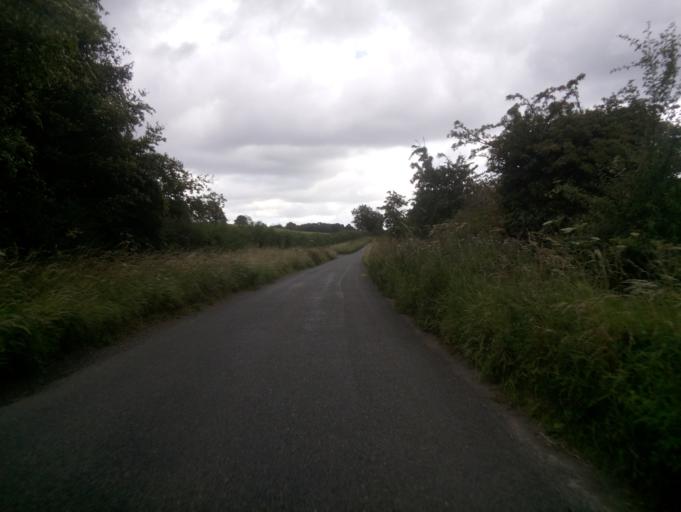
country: GB
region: England
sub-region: Gloucestershire
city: Chalford
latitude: 51.7880
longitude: -2.1132
